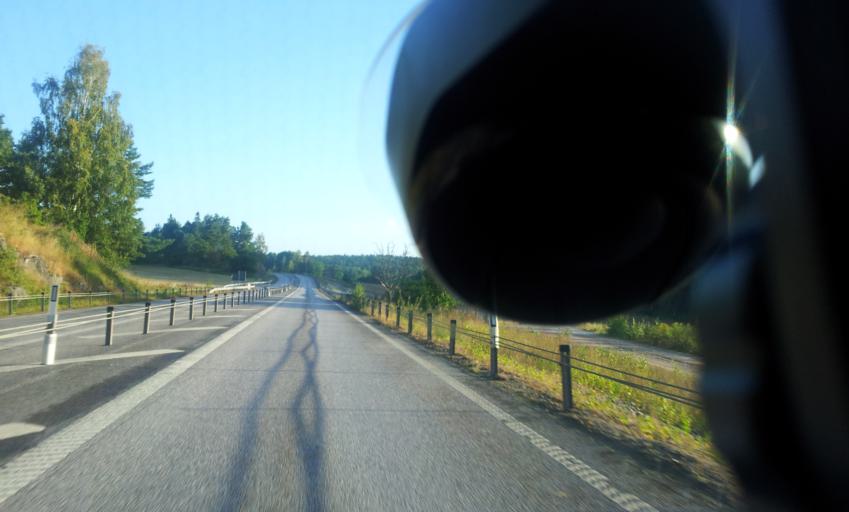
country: SE
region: Kalmar
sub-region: Vasterviks Kommun
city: Gamleby
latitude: 57.9177
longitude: 16.3999
